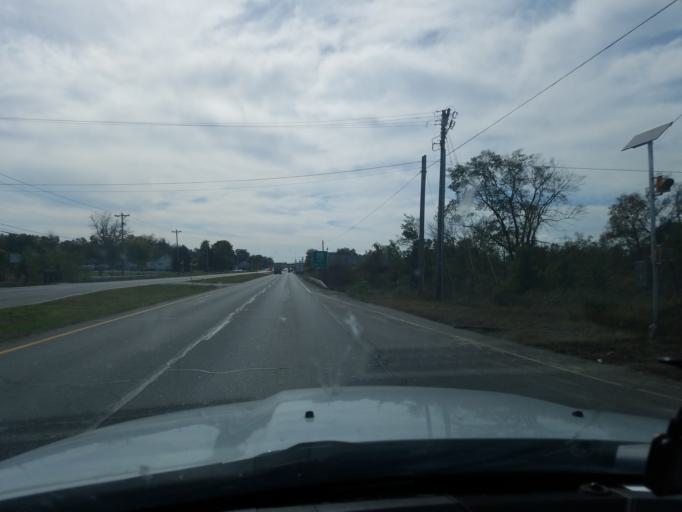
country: US
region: Indiana
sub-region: Clark County
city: Oak Park
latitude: 38.3568
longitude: -85.7022
